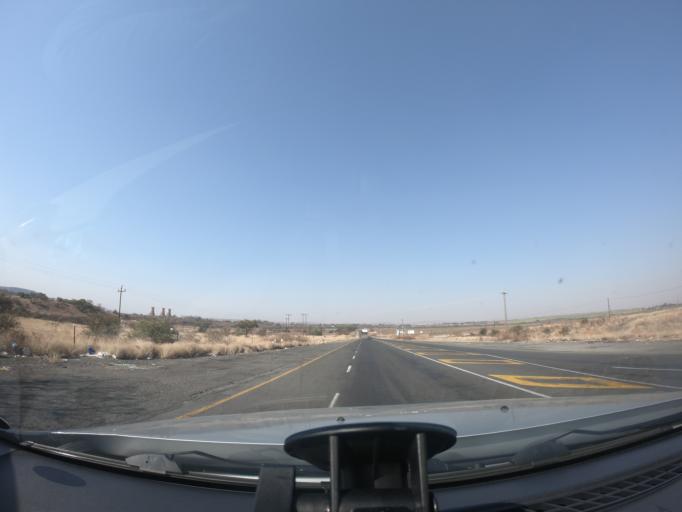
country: ZA
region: KwaZulu-Natal
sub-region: uThukela District Municipality
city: Ladysmith
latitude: -28.7282
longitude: 29.8091
